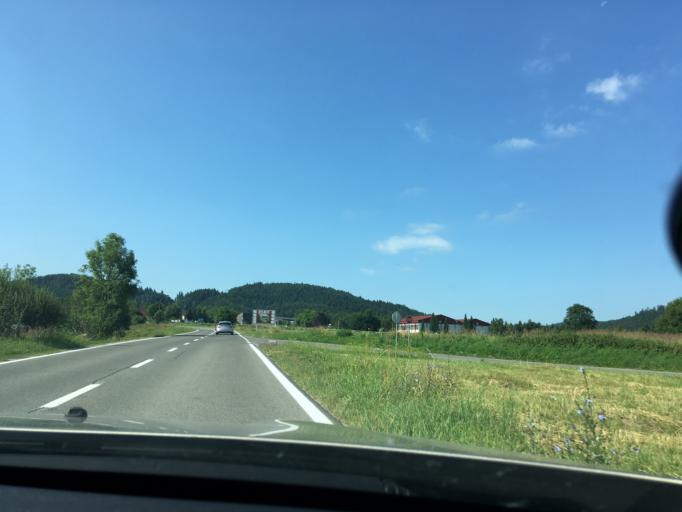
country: HR
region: Primorsko-Goranska
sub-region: Grad Delnice
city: Delnice
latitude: 45.3993
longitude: 14.8080
